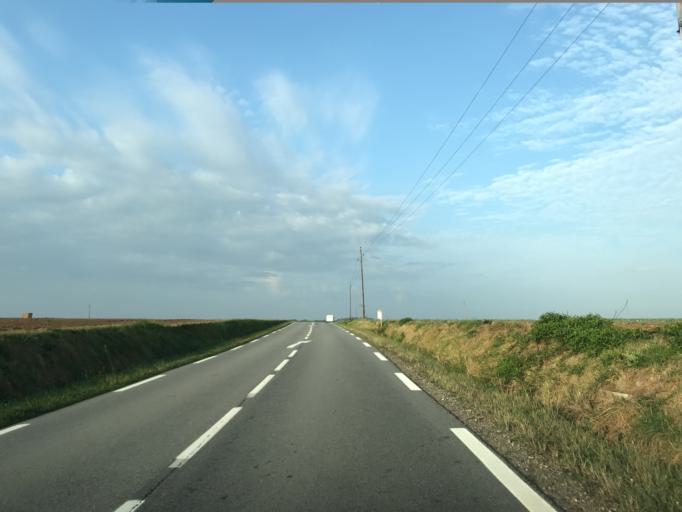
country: FR
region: Haute-Normandie
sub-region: Departement de l'Eure
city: Gravigny
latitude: 49.0697
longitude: 1.2156
